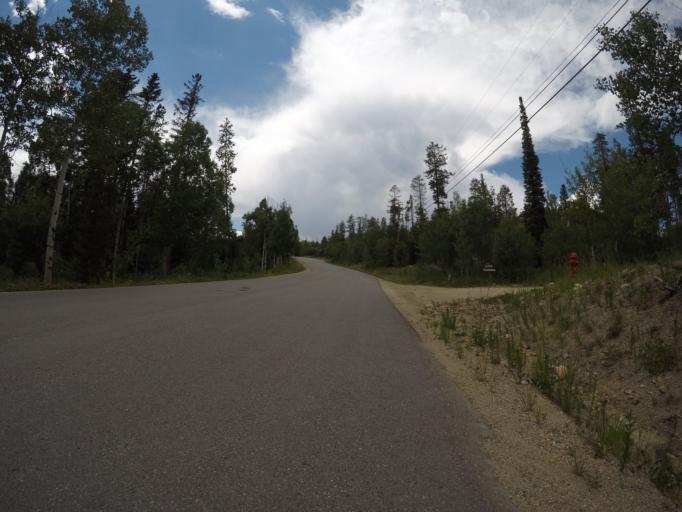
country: US
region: Colorado
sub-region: Grand County
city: Fraser
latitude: 39.9116
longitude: -105.7946
